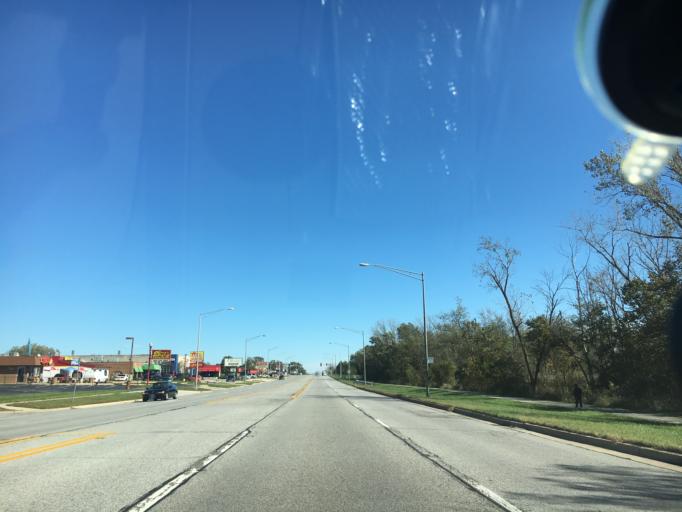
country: US
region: Illinois
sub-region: Cook County
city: Oak Forest
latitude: 41.6026
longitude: -87.7727
